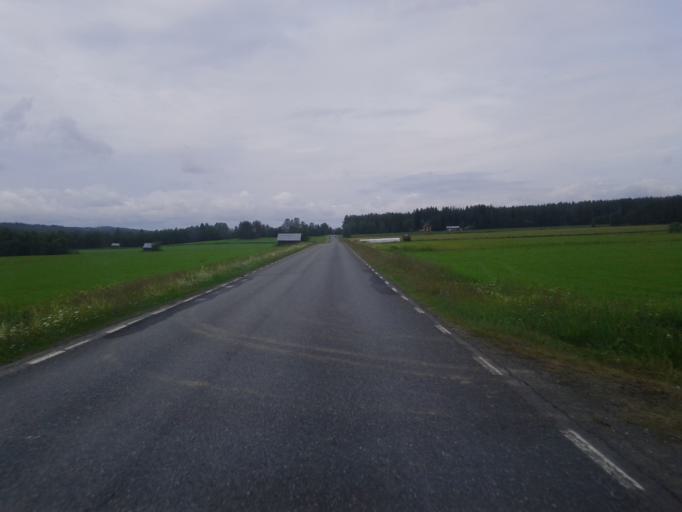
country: SE
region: Vaesterbotten
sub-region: Skelleftea Kommun
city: Viken
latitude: 64.8913
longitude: 20.7292
